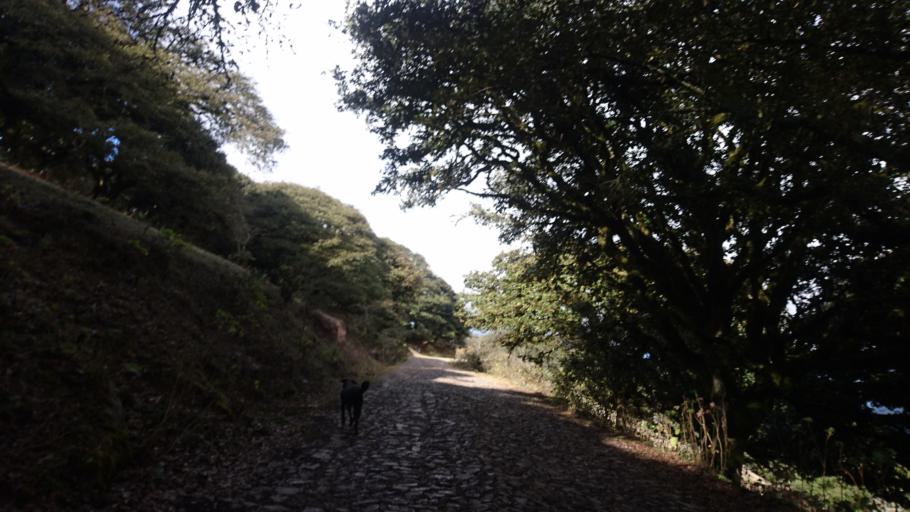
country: MX
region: San Luis Potosi
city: Zaragoza
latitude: 22.0672
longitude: -100.6389
